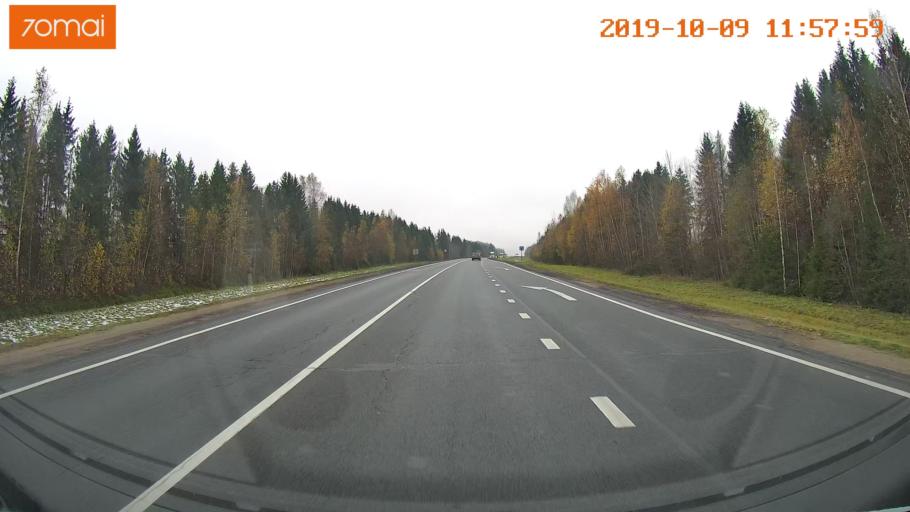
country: RU
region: Vologda
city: Gryazovets
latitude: 58.7245
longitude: 40.2956
